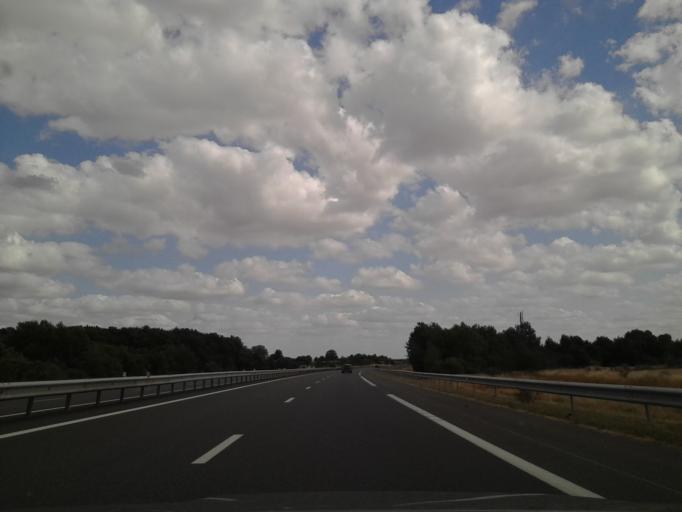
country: FR
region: Centre
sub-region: Departement du Cher
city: Saint-Amand-Montrond
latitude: 46.6346
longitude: 2.4986
